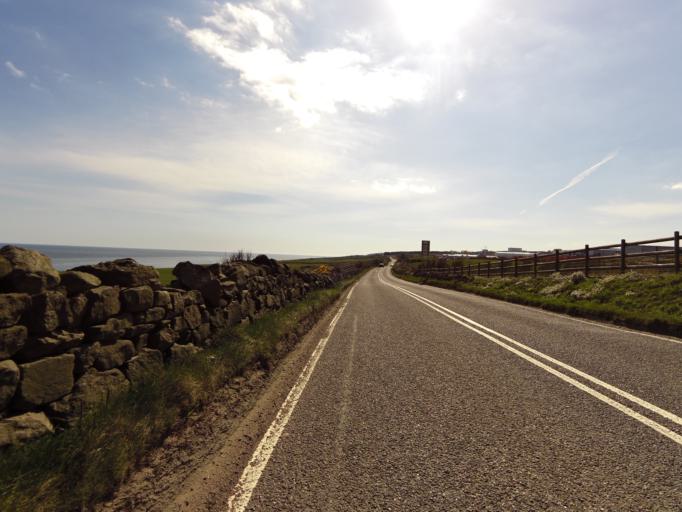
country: GB
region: Scotland
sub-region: Aberdeen City
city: Aberdeen
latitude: 57.1212
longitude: -2.0584
